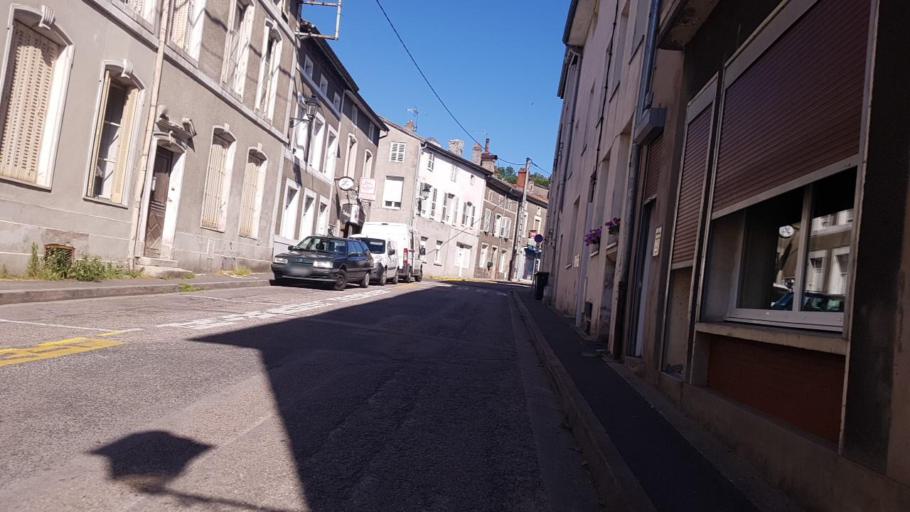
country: FR
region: Lorraine
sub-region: Departement de Meurthe-et-Moselle
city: Foug
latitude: 48.6844
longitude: 5.7874
